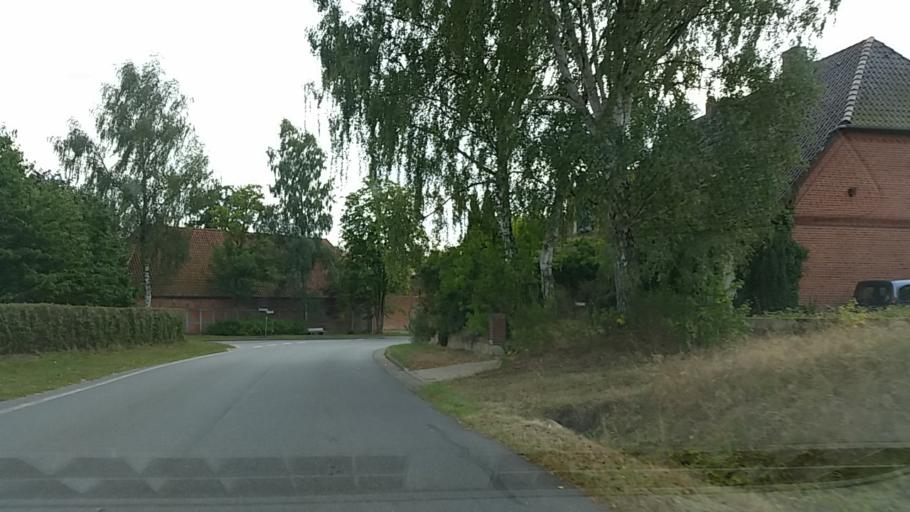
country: DE
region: Lower Saxony
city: Gerdau
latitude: 52.9726
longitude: 10.3952
